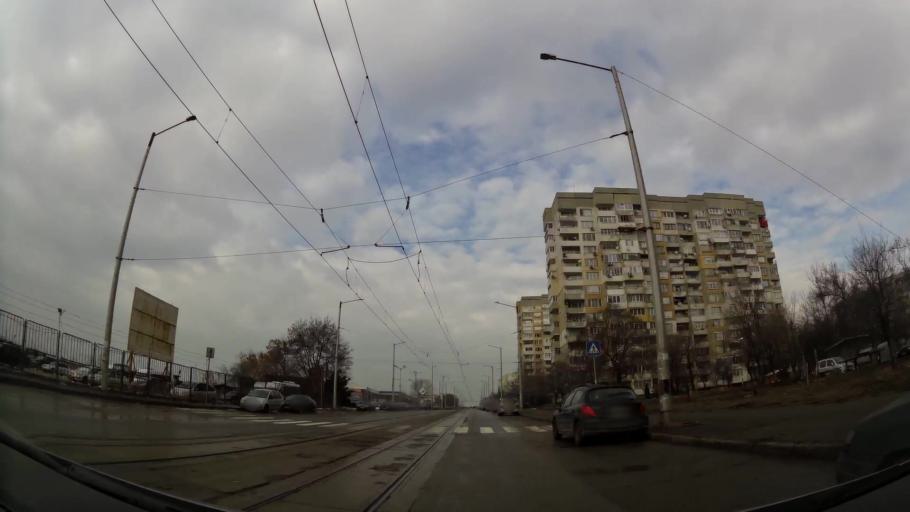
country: BG
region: Sofiya
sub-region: Obshtina Bozhurishte
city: Bozhurishte
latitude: 42.7112
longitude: 23.2424
